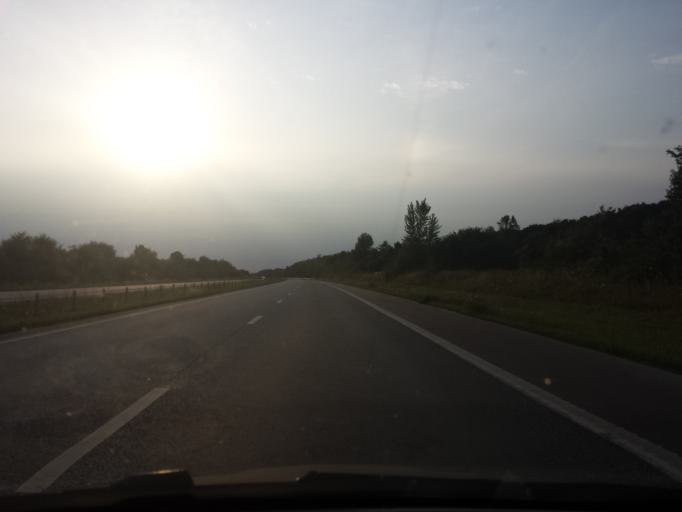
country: SE
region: Skane
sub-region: Svedala Kommun
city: Svedala
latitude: 55.5238
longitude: 13.2268
